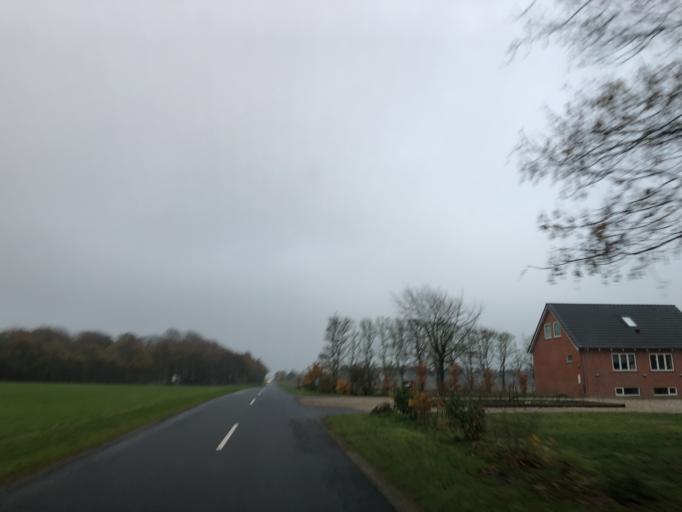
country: DK
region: Central Jutland
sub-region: Ringkobing-Skjern Kommune
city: Videbaek
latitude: 56.1907
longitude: 8.6422
